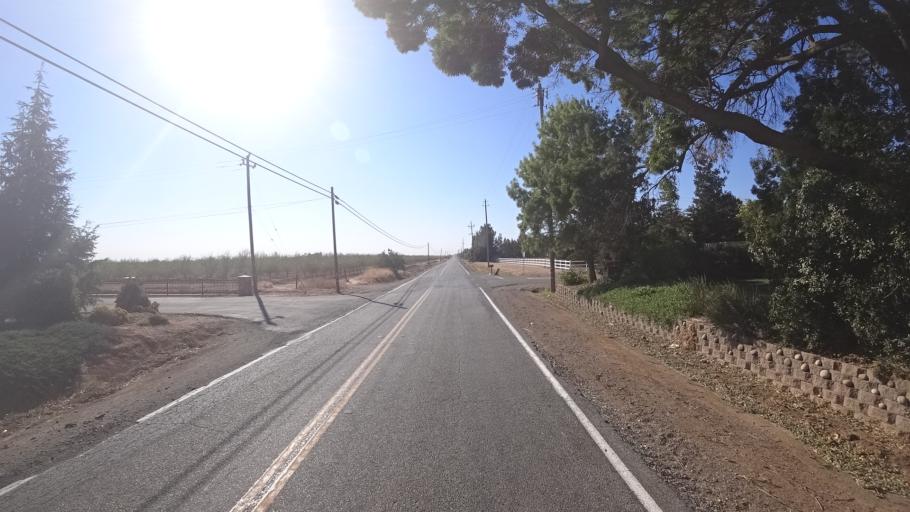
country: US
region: California
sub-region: Yolo County
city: Woodland
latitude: 38.6710
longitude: -121.8581
